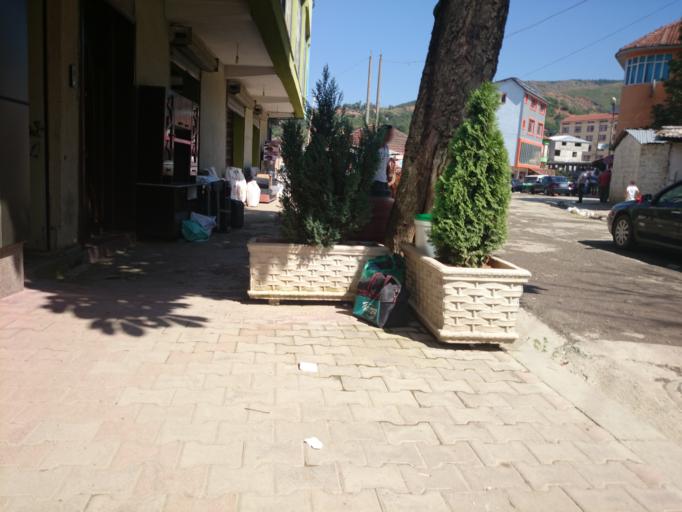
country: AL
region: Diber
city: Peshkopi
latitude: 41.6855
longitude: 20.4250
